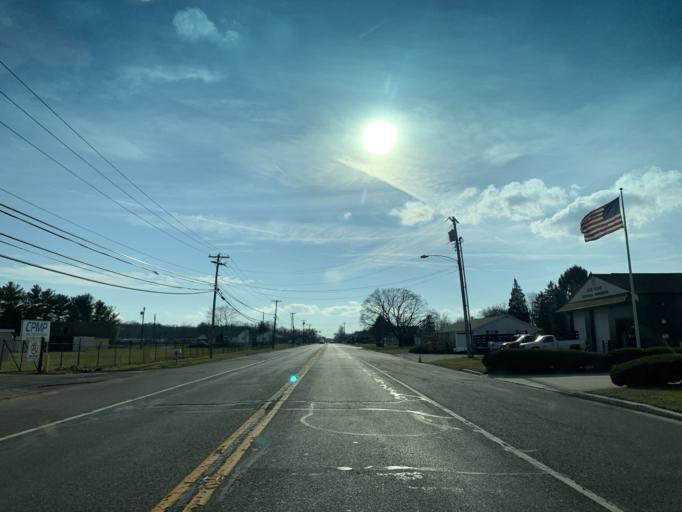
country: US
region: New Jersey
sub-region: Salem County
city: Penns Grove
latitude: 39.7432
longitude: -75.4550
